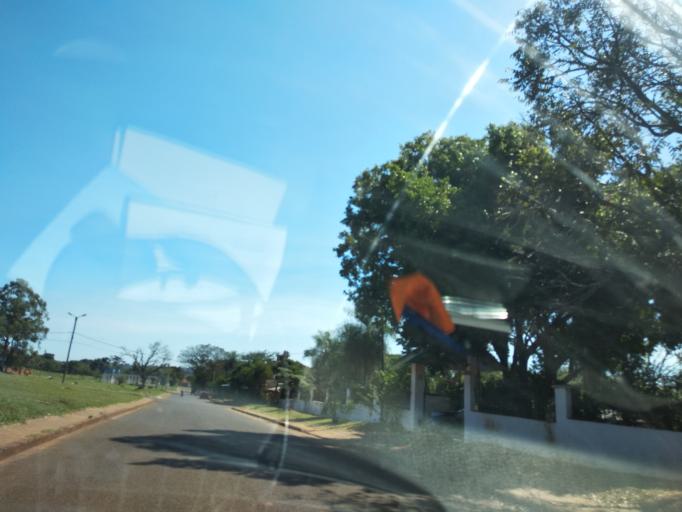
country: AR
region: Misiones
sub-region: Departamento de Capital
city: Posadas
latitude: -27.4250
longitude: -55.8819
